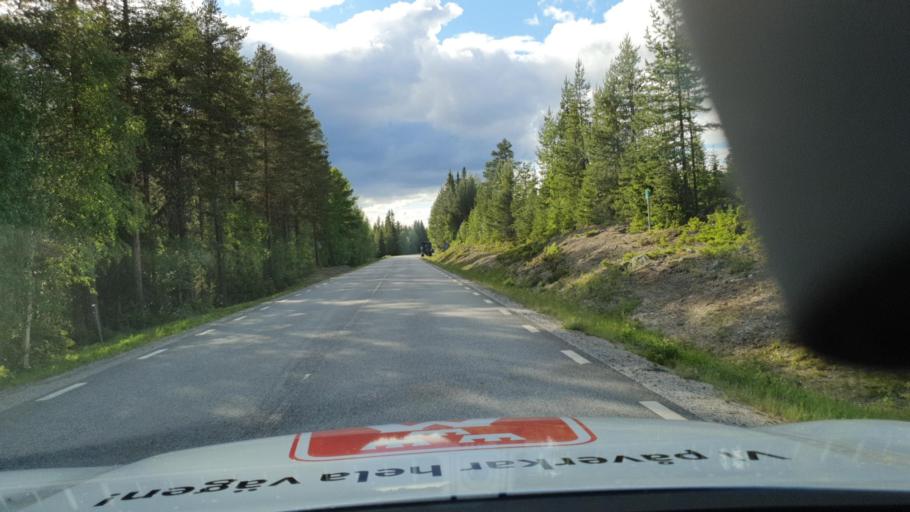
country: SE
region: Vaesterbotten
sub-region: Lycksele Kommun
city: Lycksele
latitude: 64.6795
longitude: 18.4254
